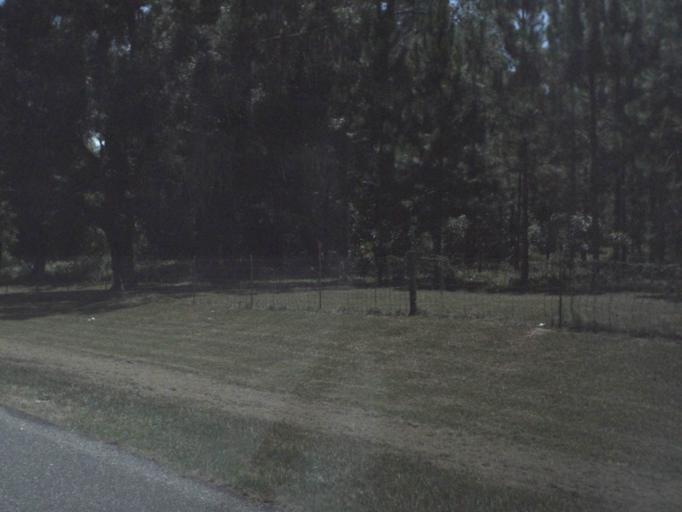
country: US
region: Florida
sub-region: Alachua County
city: High Springs
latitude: 29.9825
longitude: -82.7100
